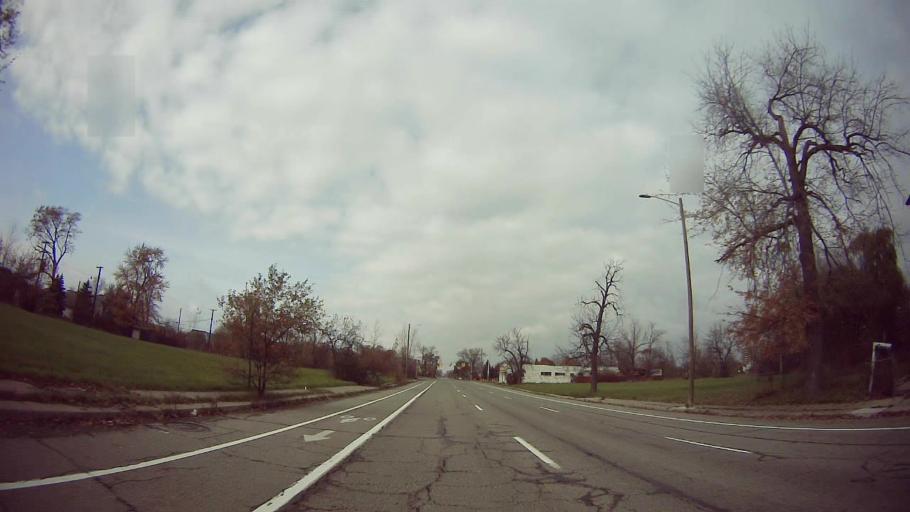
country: US
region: Michigan
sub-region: Wayne County
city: Detroit
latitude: 42.3398
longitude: -83.0813
